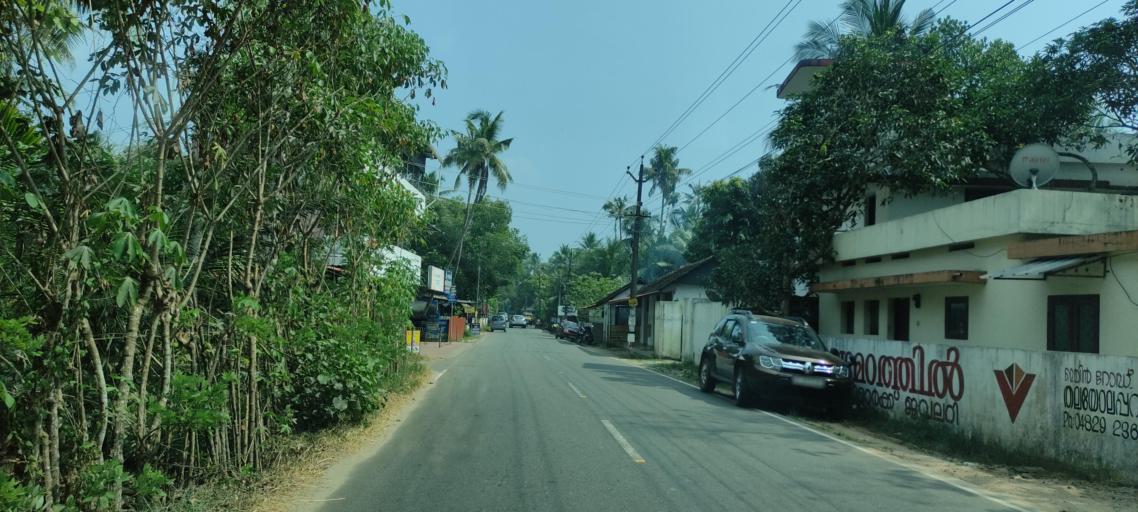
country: IN
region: Kerala
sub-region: Alappuzha
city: Shertallai
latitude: 9.6558
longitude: 76.3544
